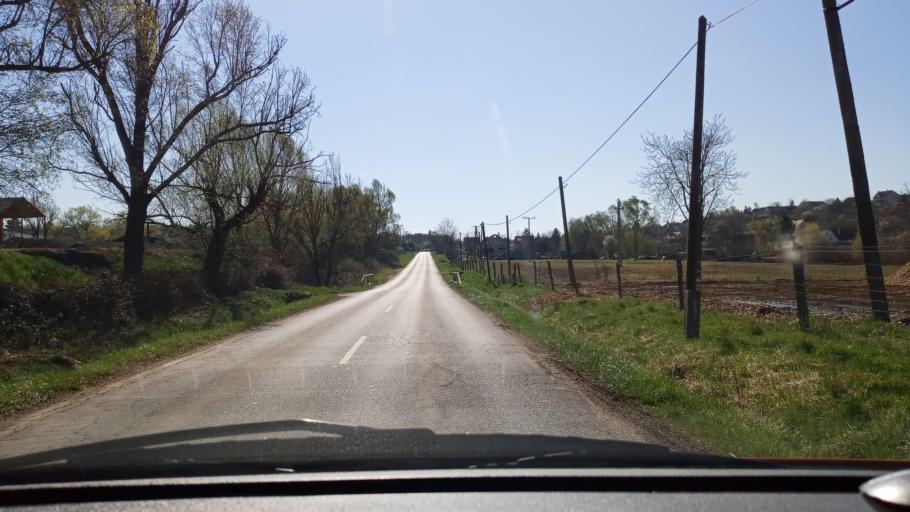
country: HU
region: Baranya
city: Pecs
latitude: 46.0892
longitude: 18.2829
